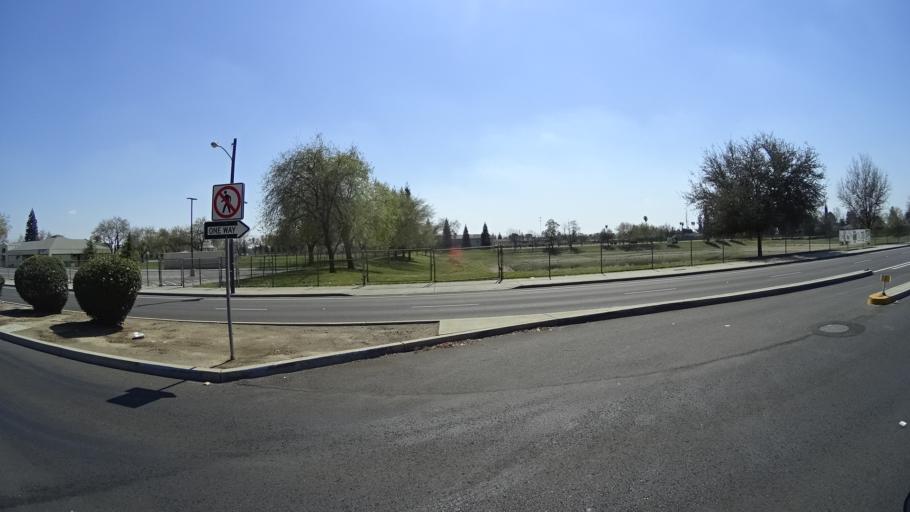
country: US
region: California
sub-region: Fresno County
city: Fresno
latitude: 36.7938
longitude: -119.8377
